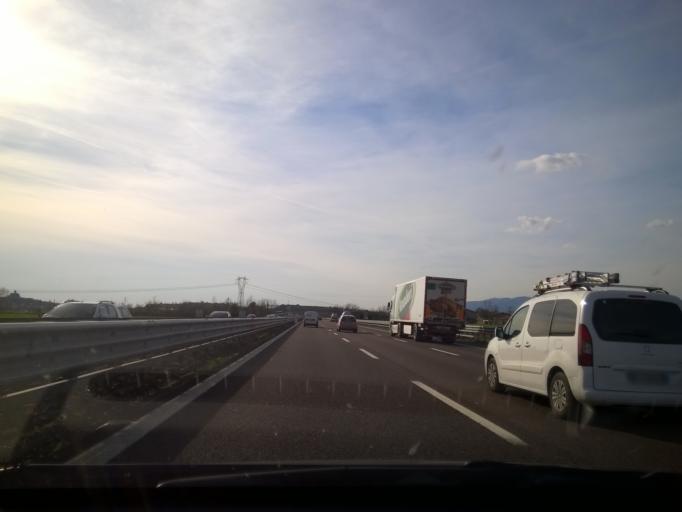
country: IT
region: Lombardy
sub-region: Provincia di Brescia
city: Lonato
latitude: 45.4605
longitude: 10.4437
